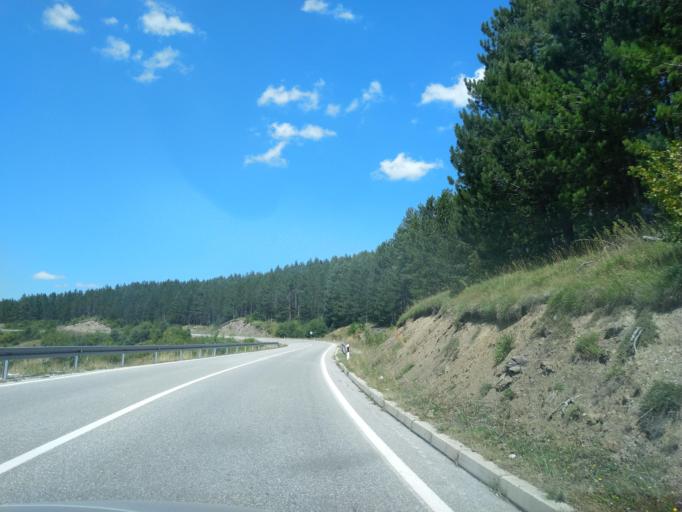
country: RS
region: Central Serbia
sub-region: Zlatiborski Okrug
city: Sjenica
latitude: 43.3028
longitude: 19.9298
